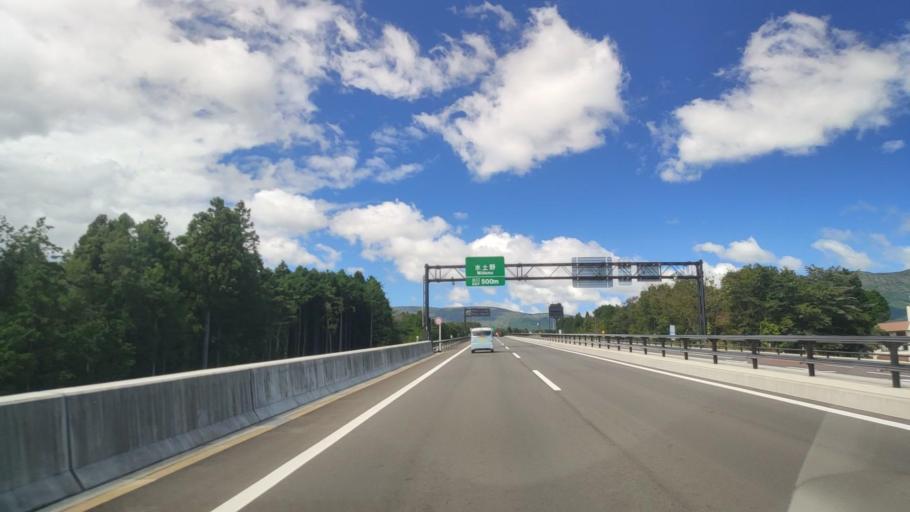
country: JP
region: Shizuoka
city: Gotemba
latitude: 35.3319
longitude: 138.8970
